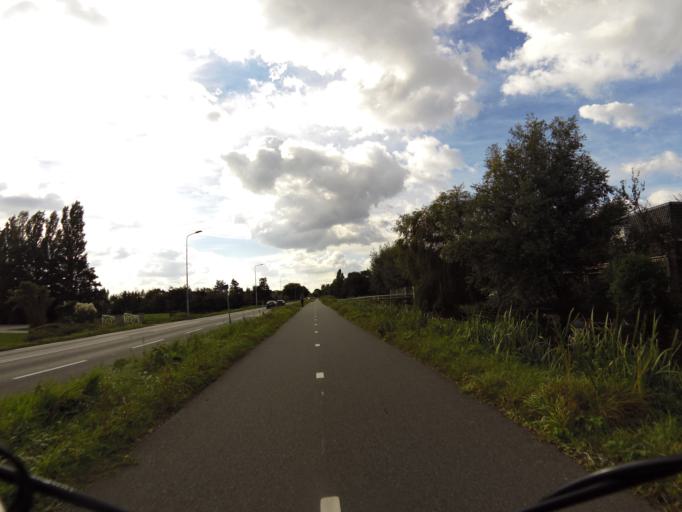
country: NL
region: South Holland
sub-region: Gemeente Voorschoten
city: Voorschoten
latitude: 52.1036
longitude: 4.4849
